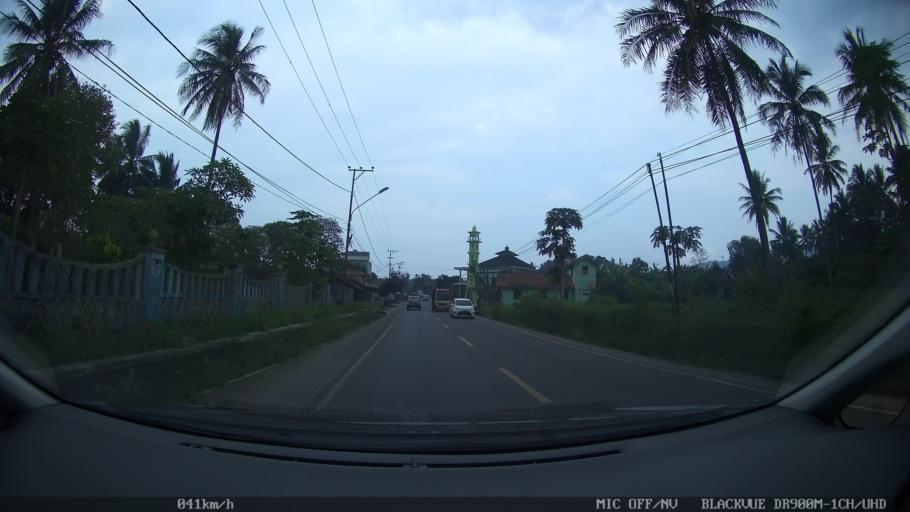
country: ID
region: Lampung
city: Gedongtataan
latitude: -5.3793
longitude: 105.1217
